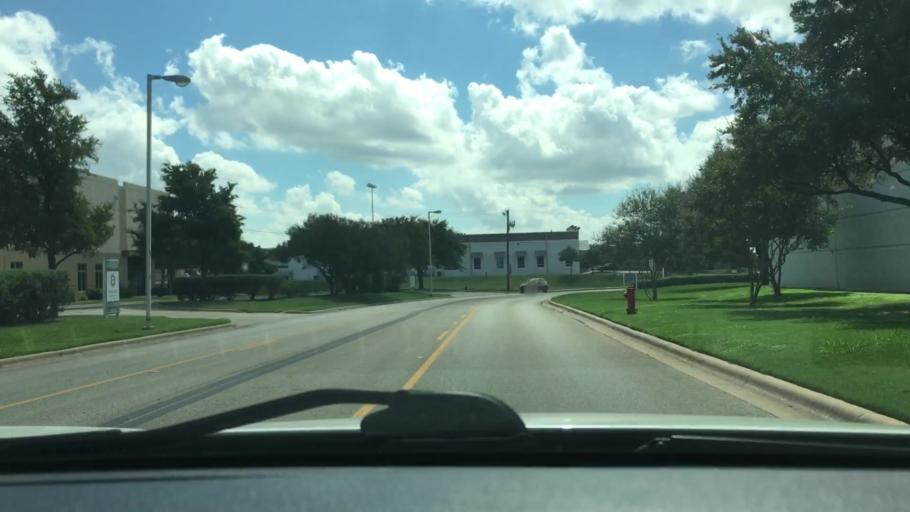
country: US
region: Texas
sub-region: Williamson County
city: Round Rock
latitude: 30.5567
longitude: -97.6851
